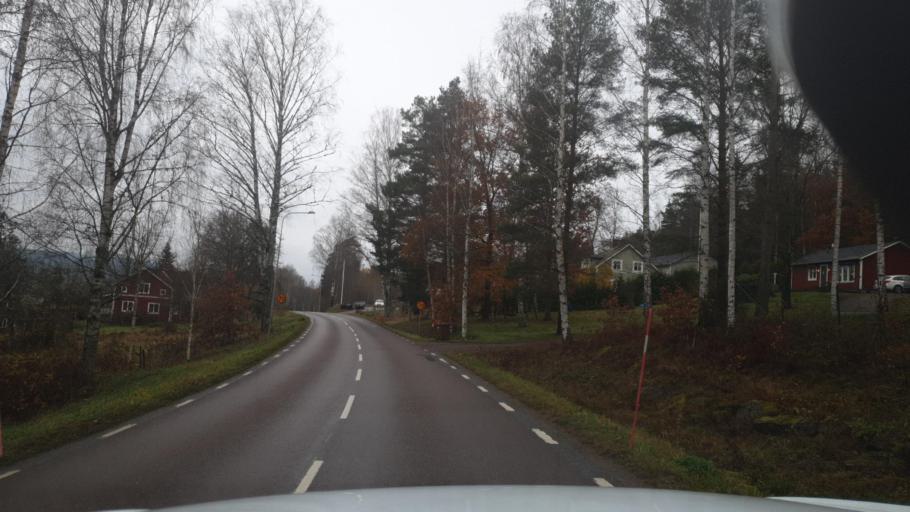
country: SE
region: Vaermland
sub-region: Arvika Kommun
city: Arvika
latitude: 59.5585
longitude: 12.5596
